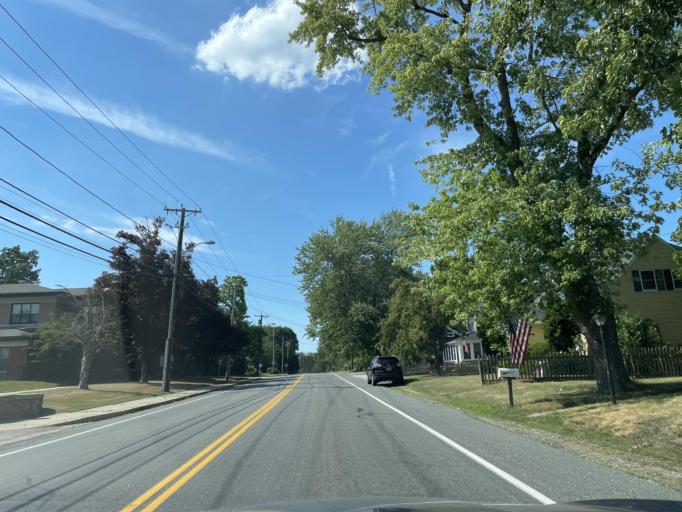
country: US
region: Massachusetts
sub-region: Worcester County
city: Mendon
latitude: 42.1091
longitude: -71.5547
